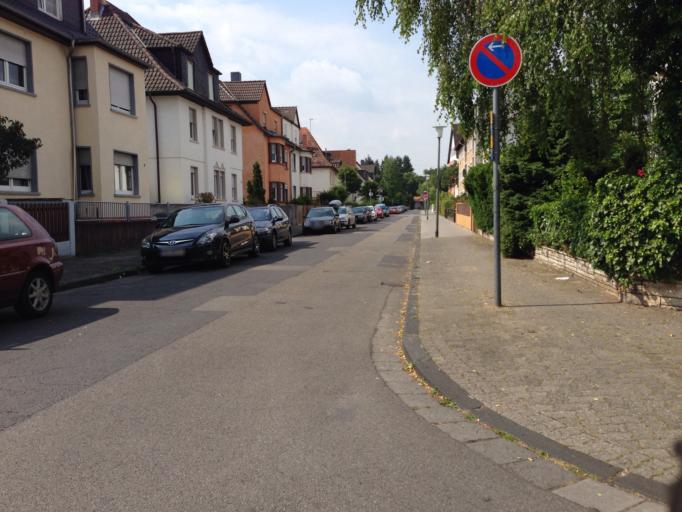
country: DE
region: Hesse
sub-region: Regierungsbezirk Darmstadt
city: Hanau am Main
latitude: 50.1279
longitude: 8.9320
